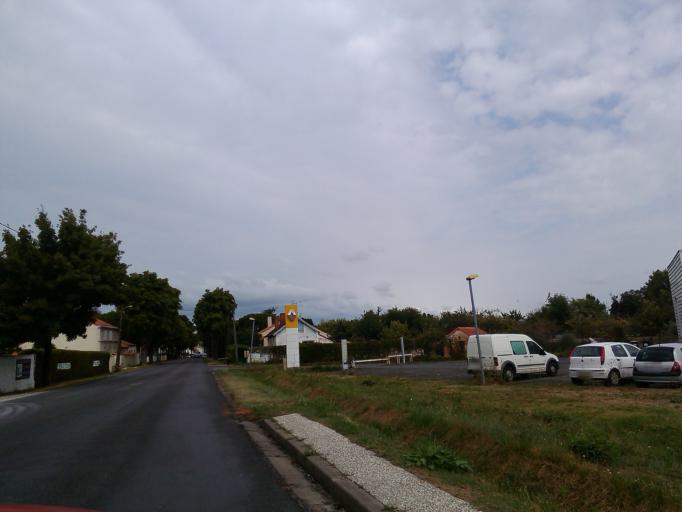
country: FR
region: Poitou-Charentes
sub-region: Departement de la Charente-Maritime
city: La Tremblade
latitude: 45.7581
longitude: -1.1404
